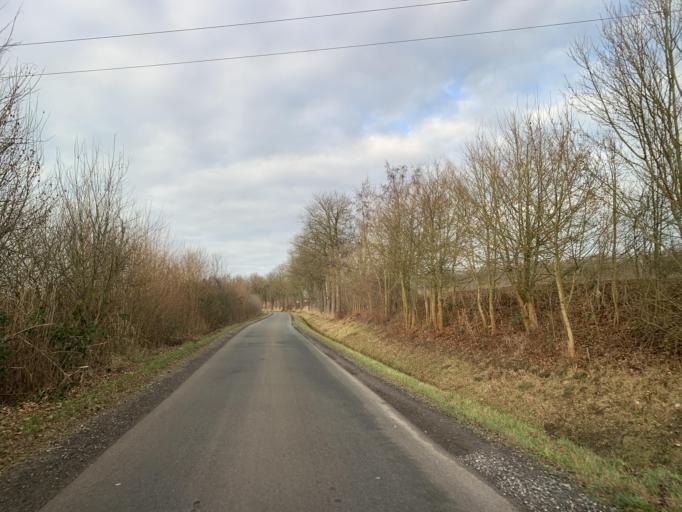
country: DE
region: North Rhine-Westphalia
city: Ludinghausen
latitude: 51.7748
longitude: 7.4134
